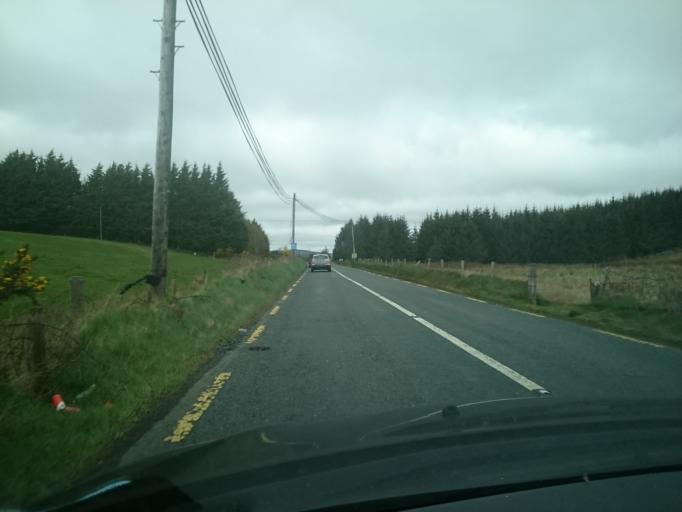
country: IE
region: Connaught
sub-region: Maigh Eo
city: Kiltamagh
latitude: 53.7922
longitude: -9.0928
